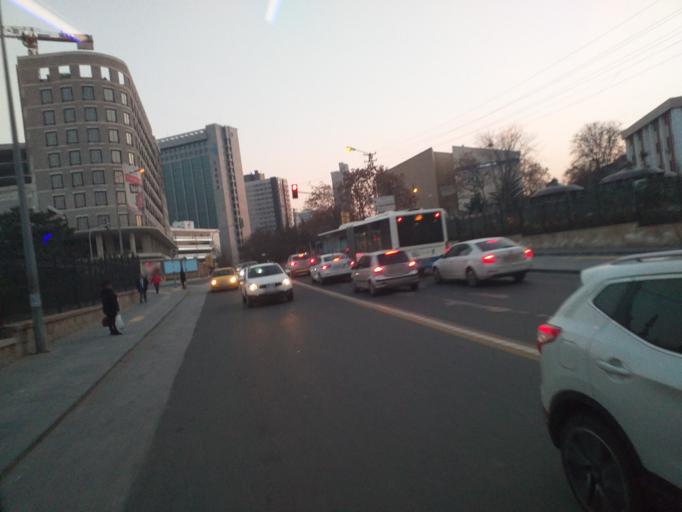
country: TR
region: Ankara
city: Ankara
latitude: 39.9428
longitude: 32.8248
